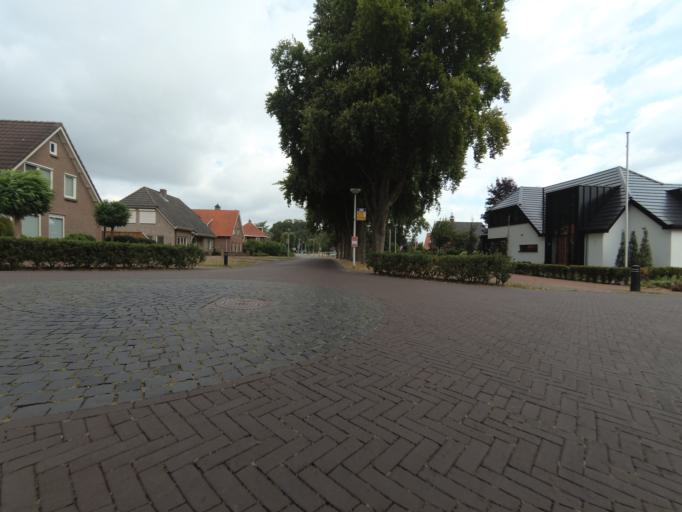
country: NL
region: Overijssel
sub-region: Gemeente Hengelo
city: Hengelo
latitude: 52.3028
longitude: 6.8379
